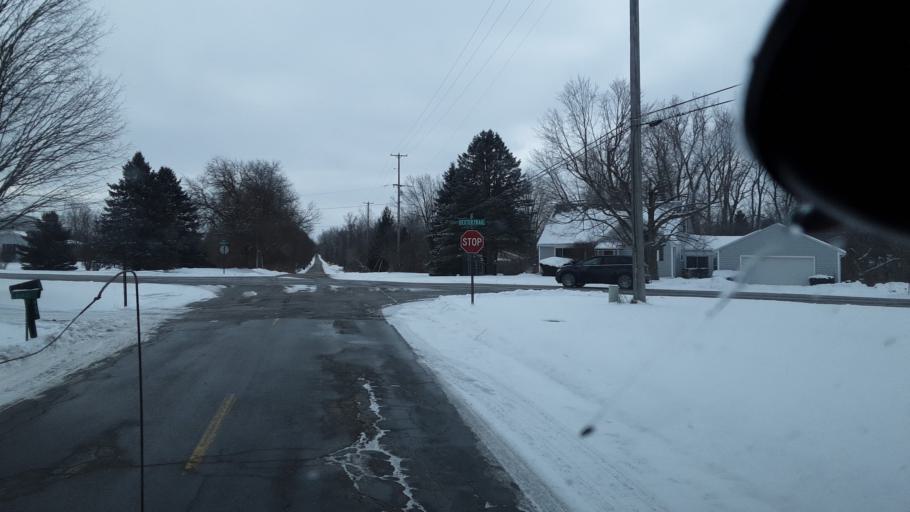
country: US
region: Michigan
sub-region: Ingham County
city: Mason
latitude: 42.5575
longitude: -84.4036
